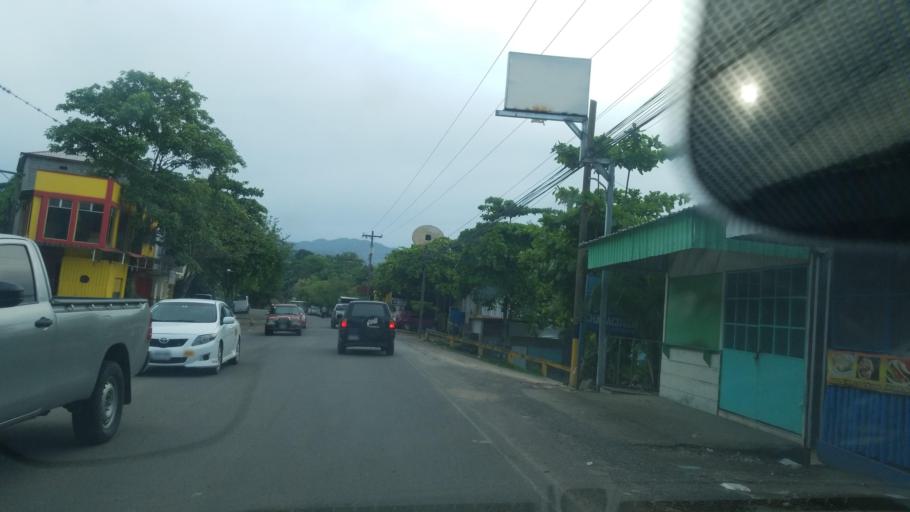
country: HN
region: Santa Barbara
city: Santa Barbara
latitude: 14.9203
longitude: -88.2448
